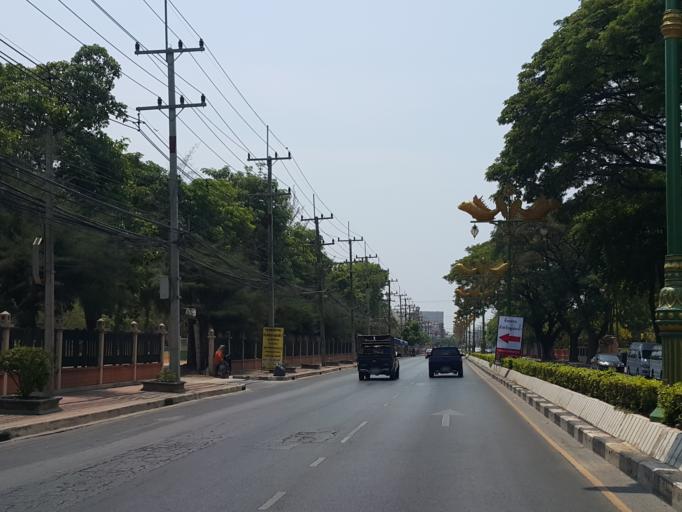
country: TH
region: Kanchanaburi
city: Kanchanaburi
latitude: 14.0321
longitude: 99.5258
